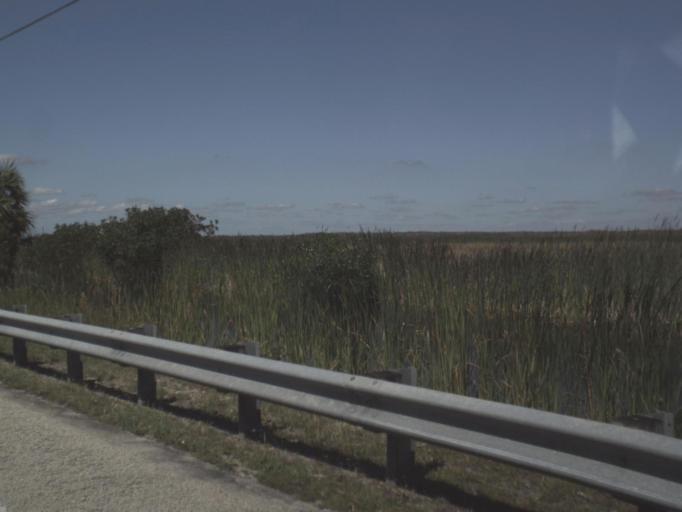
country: US
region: Florida
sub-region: Collier County
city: Marco
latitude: 25.9185
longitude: -81.3902
